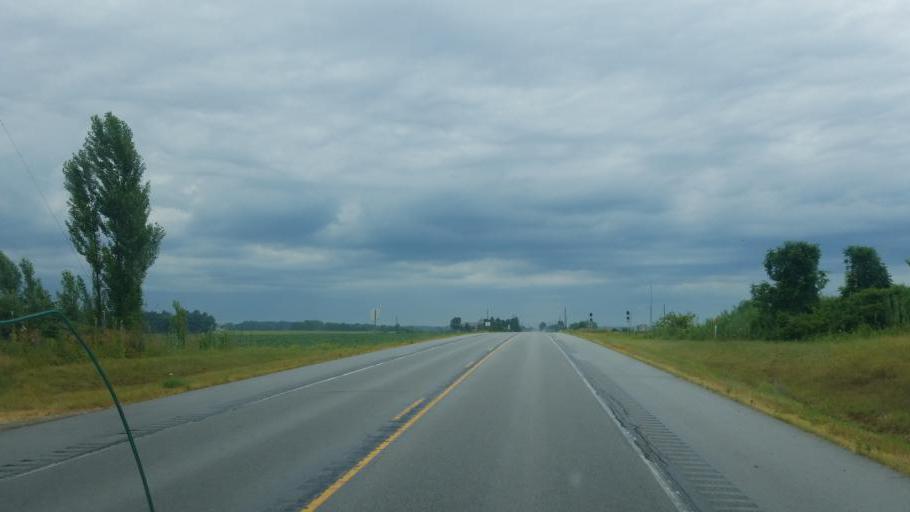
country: US
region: Ohio
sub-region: Williams County
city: Edgerton
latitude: 41.4381
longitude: -84.8076
